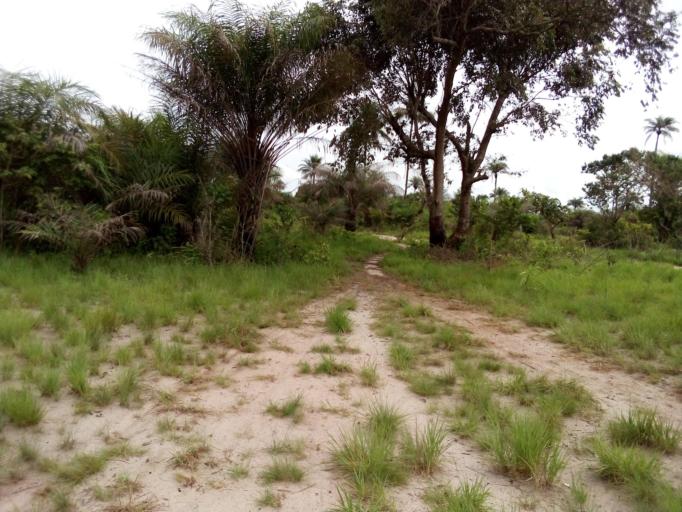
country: SL
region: Southern Province
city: Bonthe
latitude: 7.5212
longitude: -12.5761
